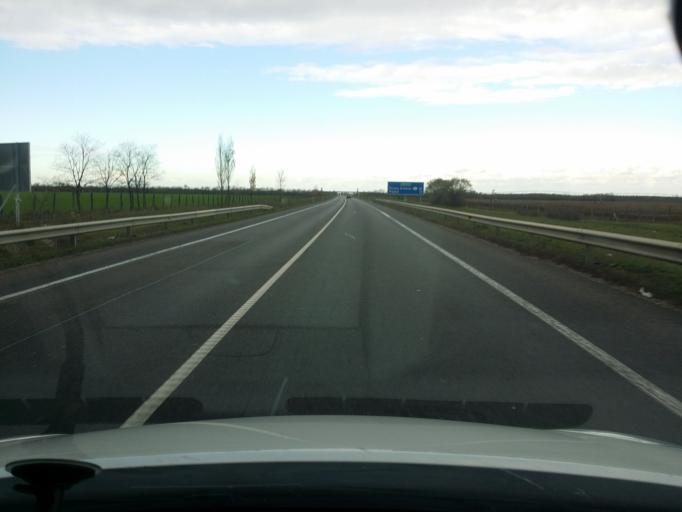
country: HU
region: Gyor-Moson-Sopron
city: Rajka
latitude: 47.9144
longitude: 17.1803
